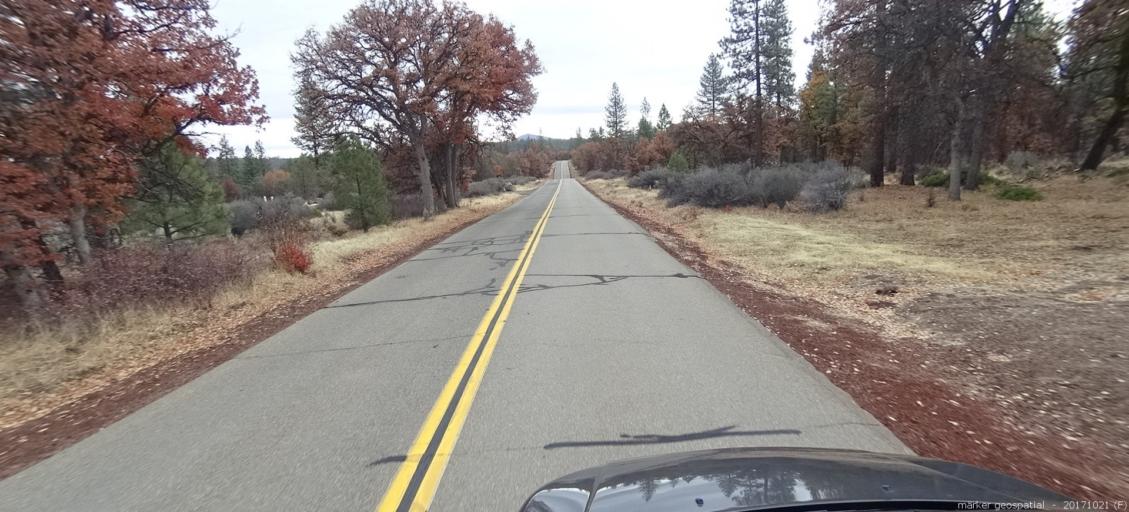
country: US
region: California
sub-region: Shasta County
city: Burney
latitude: 40.9328
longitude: -121.5630
